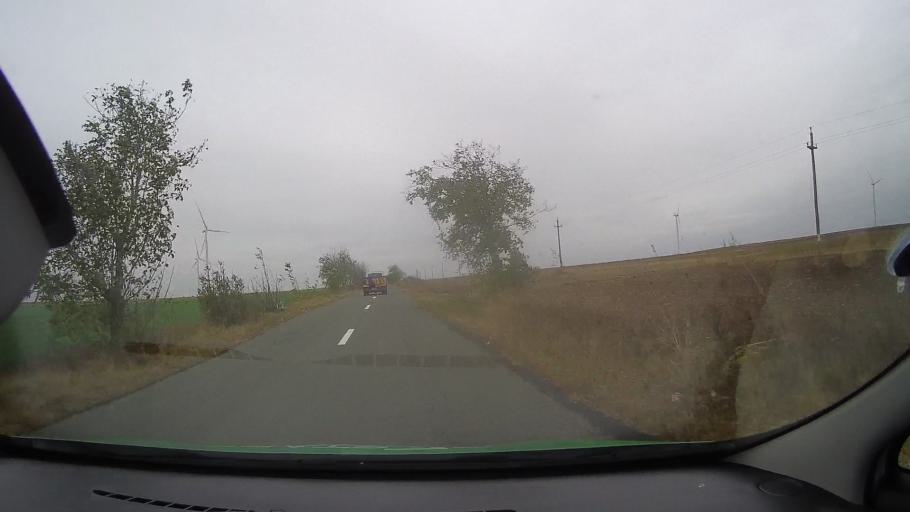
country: RO
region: Constanta
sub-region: Comuna Targusor
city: Targusor
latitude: 44.4764
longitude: 28.3794
